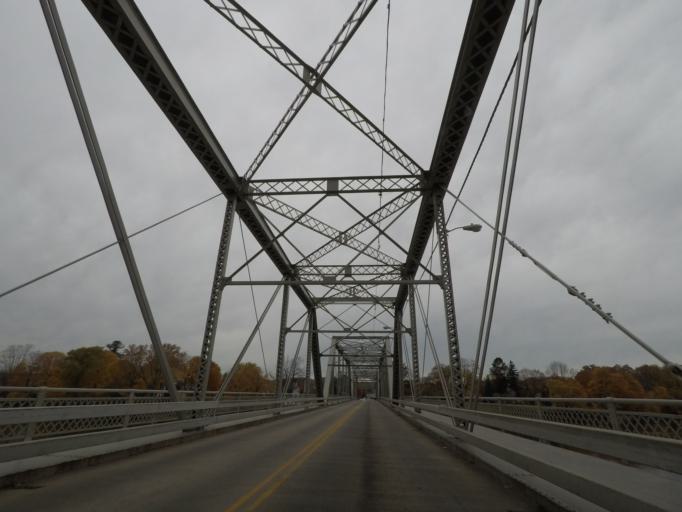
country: US
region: New York
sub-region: Saratoga County
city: Waterford
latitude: 42.7885
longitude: -73.6734
